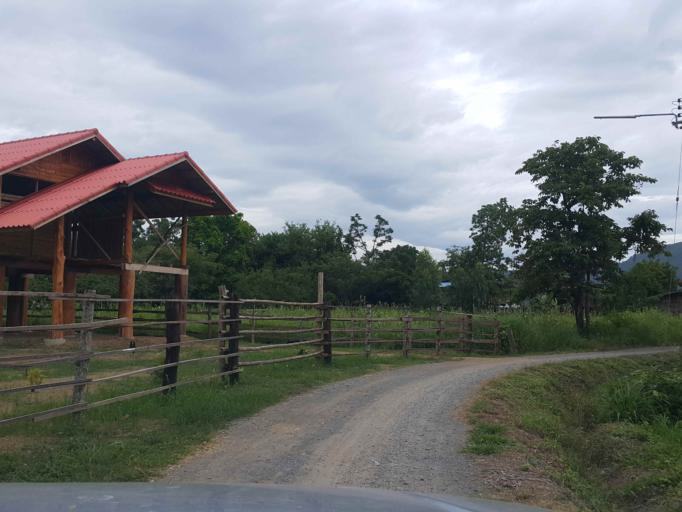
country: TH
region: Sukhothai
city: Thung Saliam
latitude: 17.3253
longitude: 99.4420
